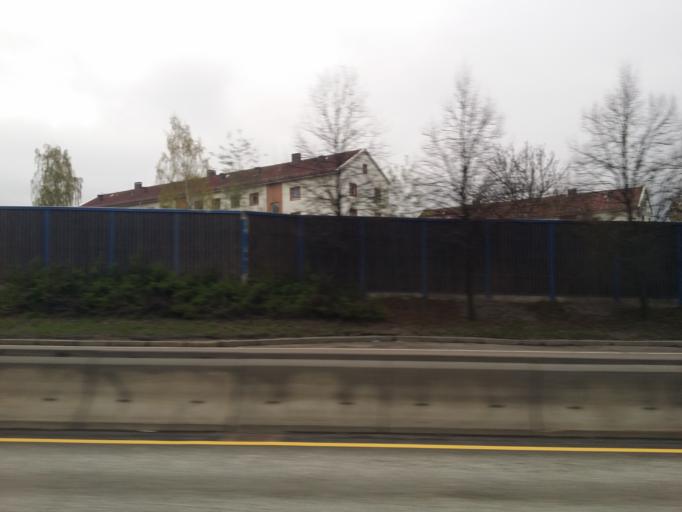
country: NO
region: Oslo
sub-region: Oslo
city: Oslo
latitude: 59.9120
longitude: 10.7972
